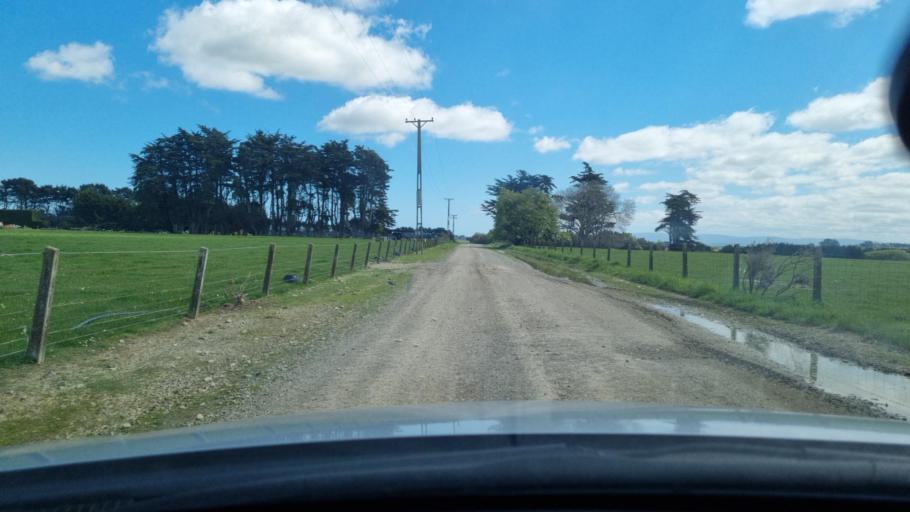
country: NZ
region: Southland
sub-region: Invercargill City
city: Invercargill
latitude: -46.3509
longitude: 168.3081
